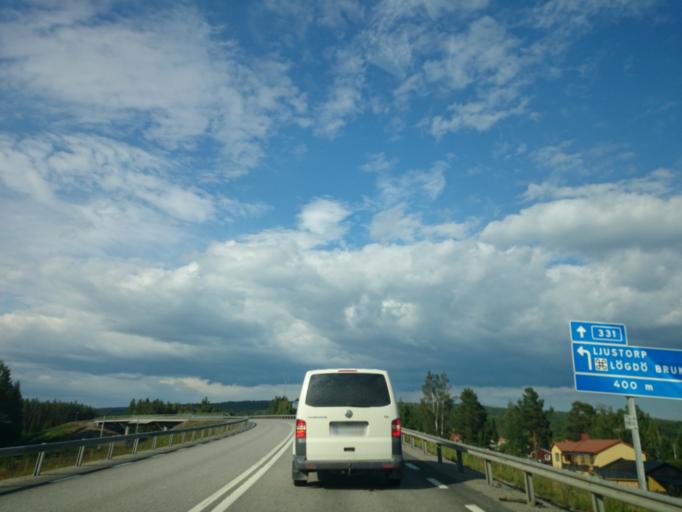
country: SE
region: Vaesternorrland
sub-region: Timra Kommun
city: Bergeforsen
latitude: 62.5505
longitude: 17.4025
